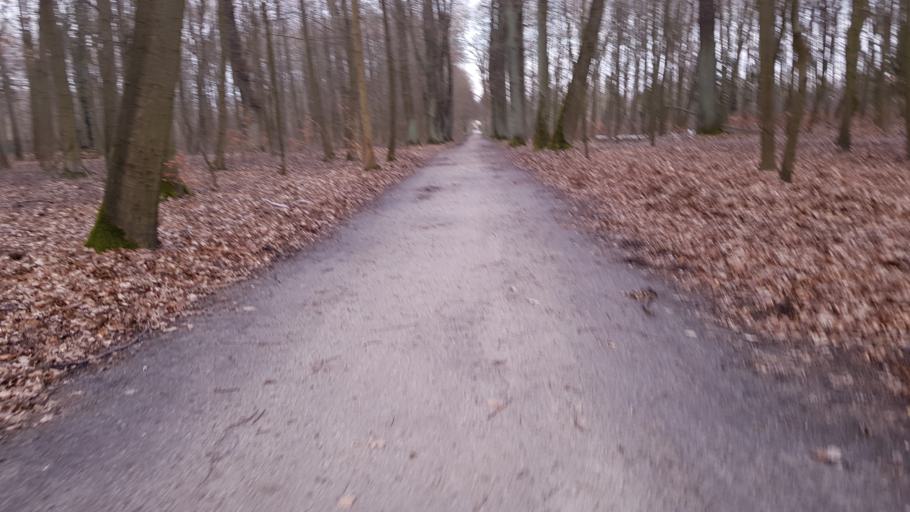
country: DE
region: Brandenburg
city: Finsterwalde
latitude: 51.6277
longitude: 13.6881
